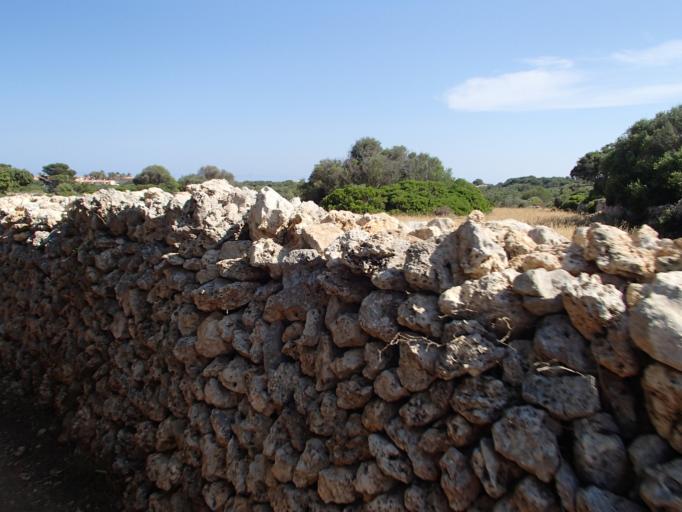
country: ES
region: Balearic Islands
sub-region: Illes Balears
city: Es Castell
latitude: 39.8435
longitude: 4.2938
